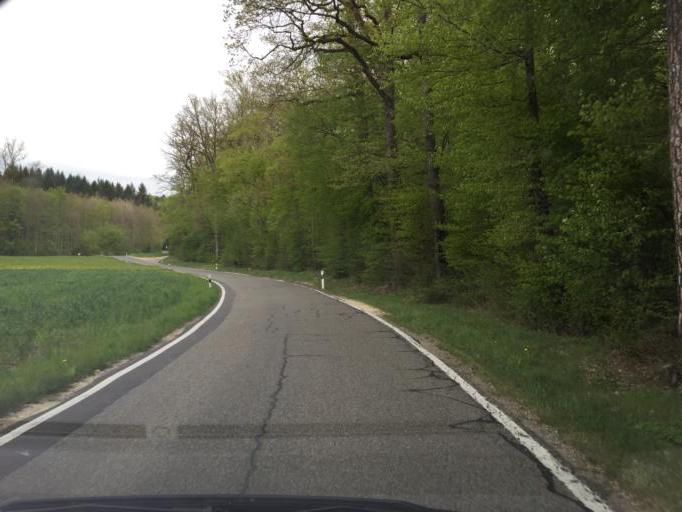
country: DE
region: Baden-Wuerttemberg
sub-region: Freiburg Region
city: Busingen
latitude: 47.7036
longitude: 8.6841
